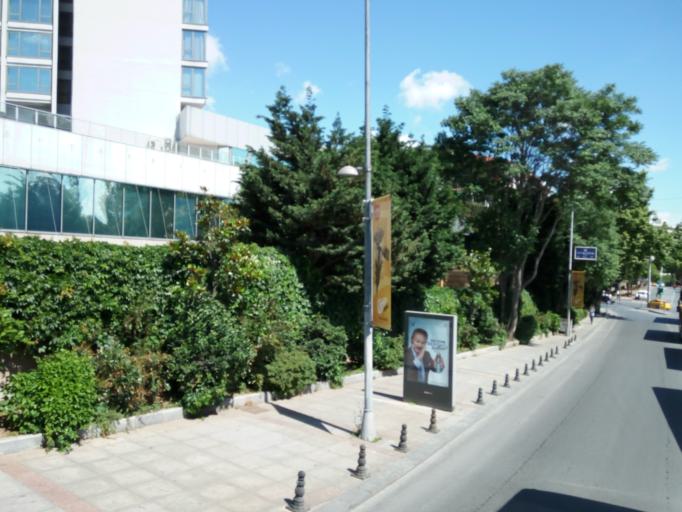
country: TR
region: Istanbul
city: Sisli
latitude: 41.0392
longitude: 28.9886
